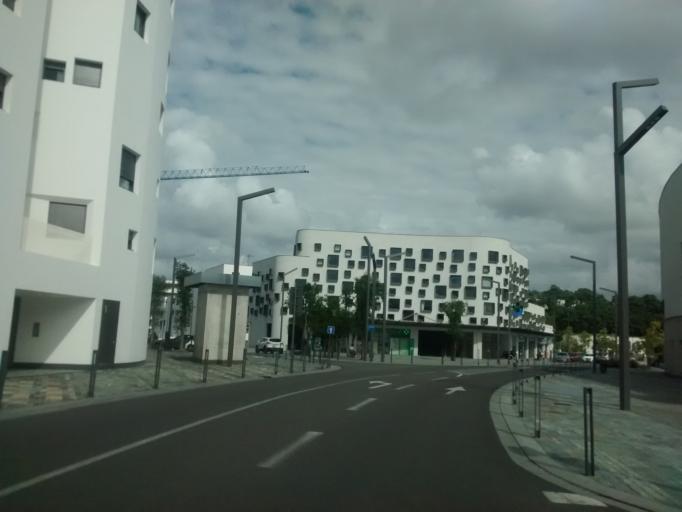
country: FR
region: Aquitaine
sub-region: Departement des Pyrenees-Atlantiques
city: Biarritz
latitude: 43.4767
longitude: -1.5490
